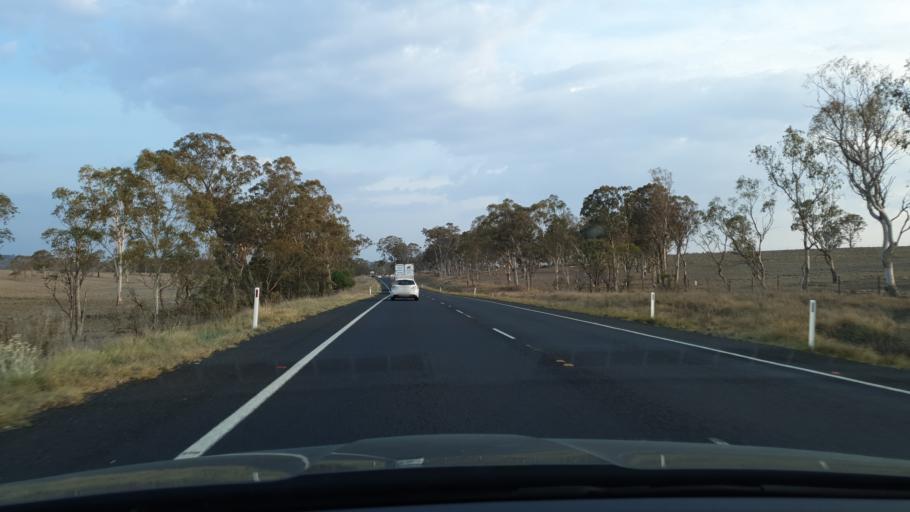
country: AU
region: New South Wales
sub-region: Glen Innes Severn
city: Glen Innes
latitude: -29.4894
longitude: 151.8583
